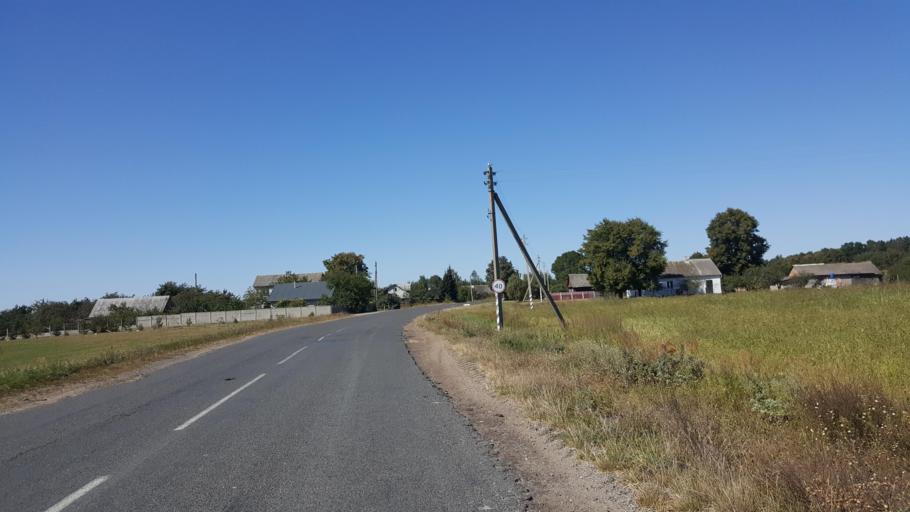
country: PL
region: Lublin Voivodeship
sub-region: Powiat bialski
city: Terespol
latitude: 52.2129
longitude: 23.5154
